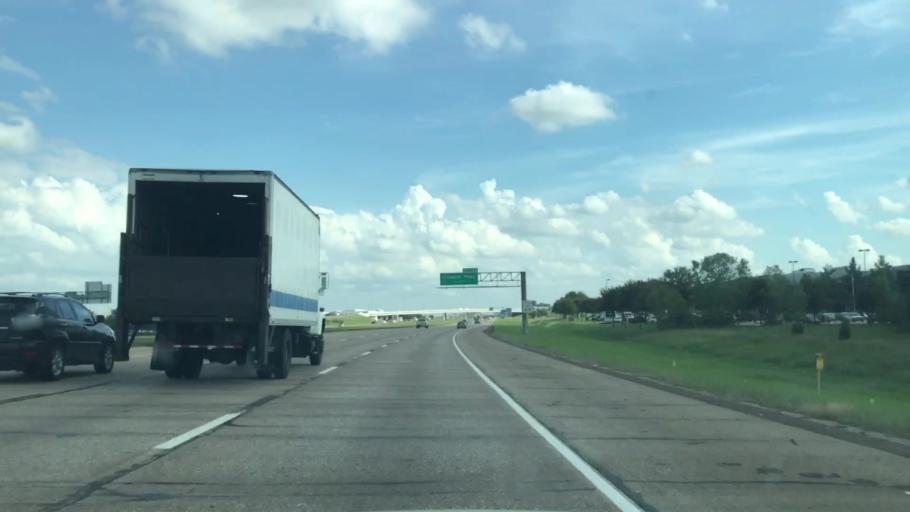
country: US
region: Texas
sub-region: Dallas County
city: Coppell
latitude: 32.9403
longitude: -97.0133
